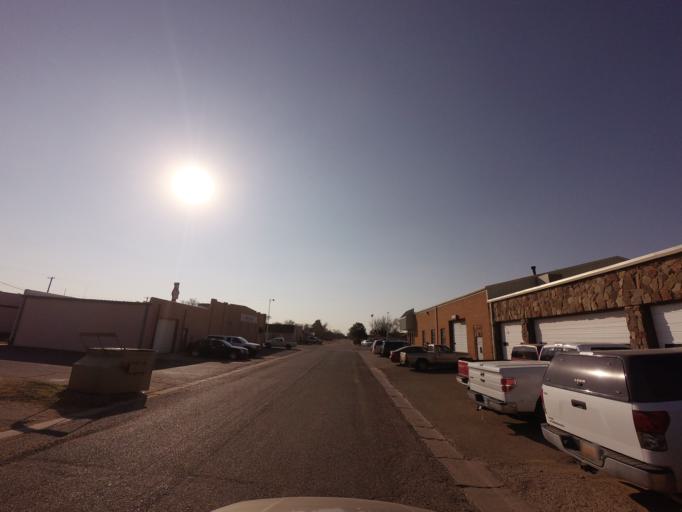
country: US
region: New Mexico
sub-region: Curry County
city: Clovis
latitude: 34.4053
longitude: -103.2117
